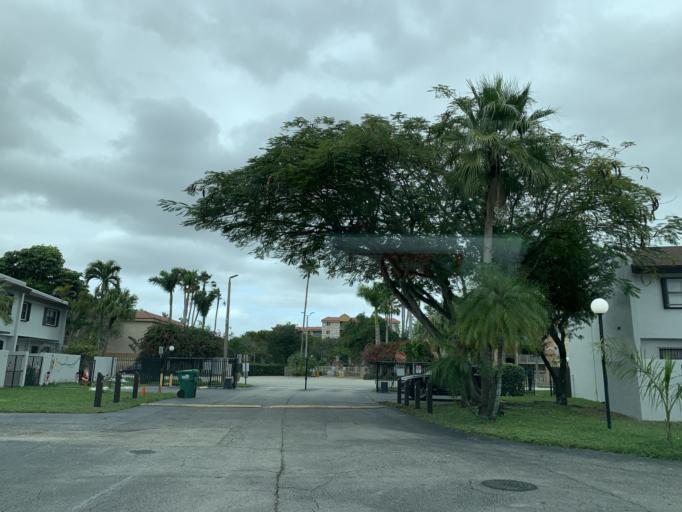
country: US
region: Florida
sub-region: Miami-Dade County
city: Kendall West
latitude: 25.6922
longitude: -80.4402
